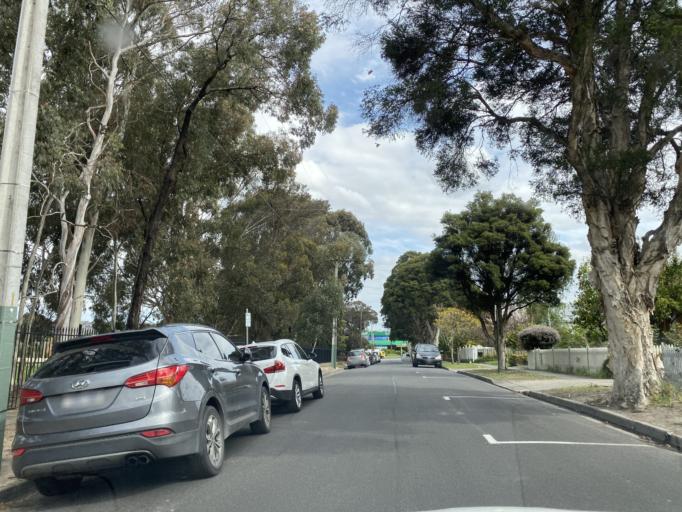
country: AU
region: Victoria
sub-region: Whitehorse
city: Burwood
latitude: -37.8487
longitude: 145.1038
